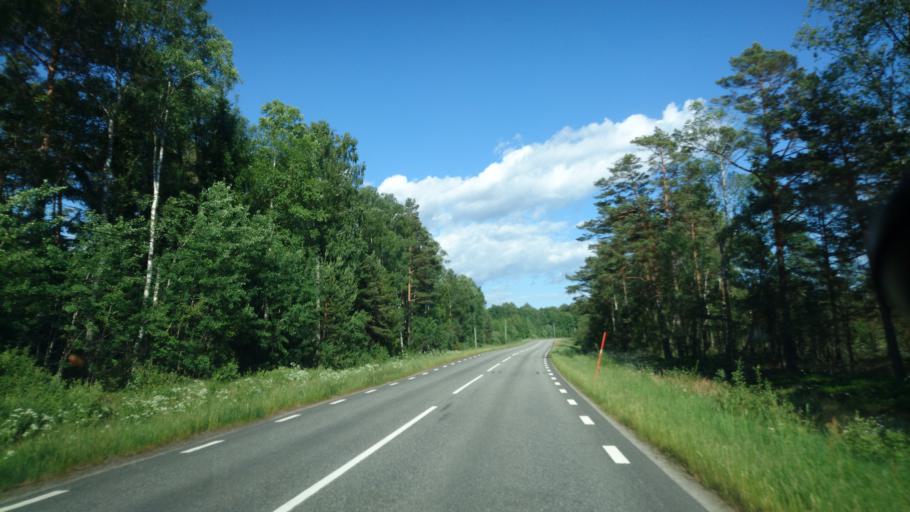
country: SE
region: Kronoberg
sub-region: Almhults Kommun
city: AElmhult
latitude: 56.4838
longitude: 14.1795
